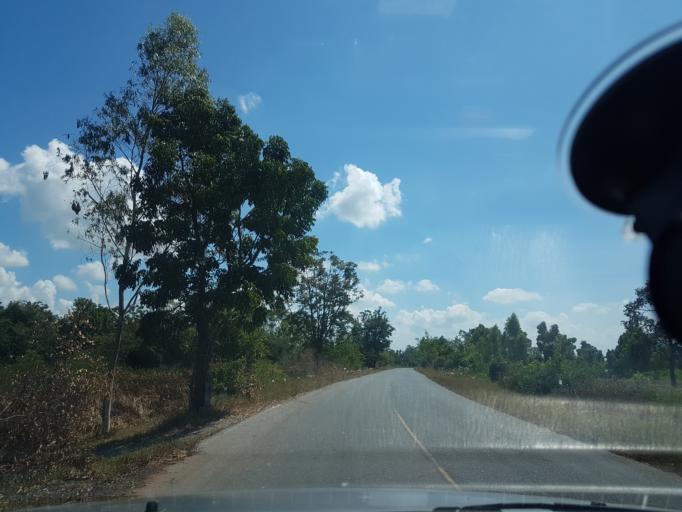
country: TH
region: Lop Buri
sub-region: Amphoe Tha Luang
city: Tha Luang
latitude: 15.0023
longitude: 101.0043
